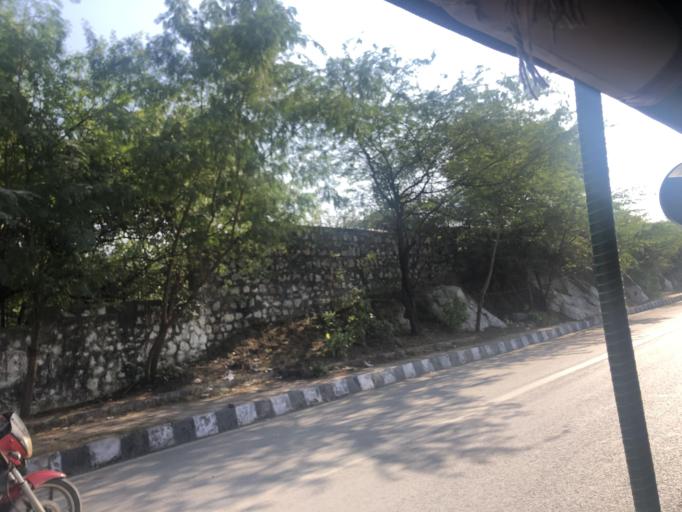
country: IN
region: NCT
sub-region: Central Delhi
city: Karol Bagh
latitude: 28.5471
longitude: 77.1618
